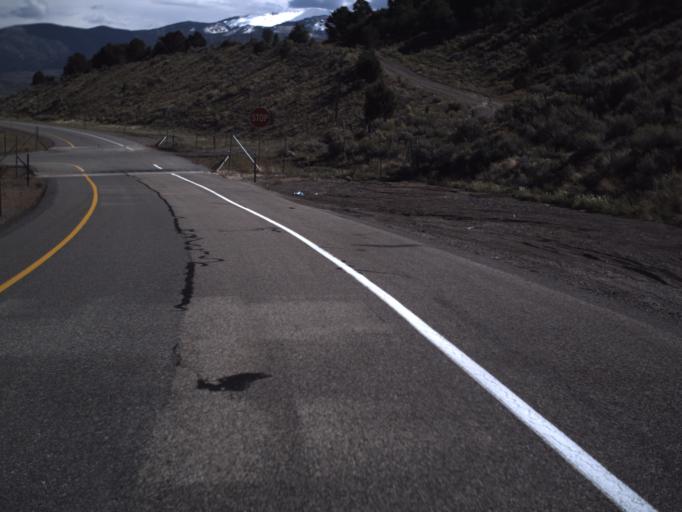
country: US
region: Utah
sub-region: Beaver County
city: Beaver
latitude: 38.5875
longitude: -112.4909
